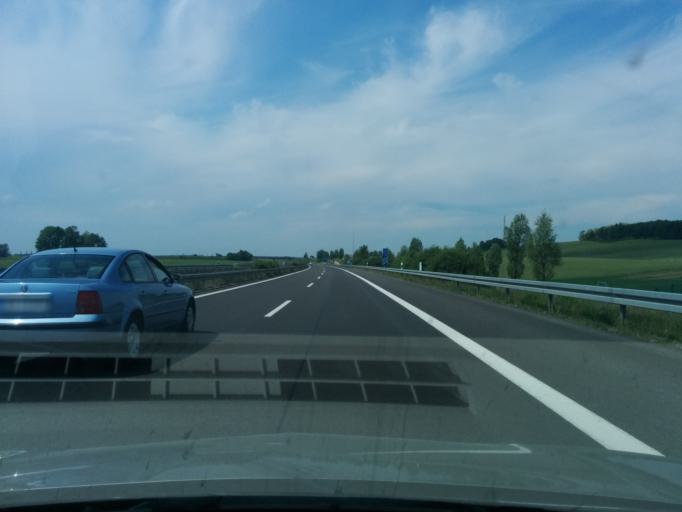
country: DE
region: Mecklenburg-Vorpommern
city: Strasburg
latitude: 53.5412
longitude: 13.7150
